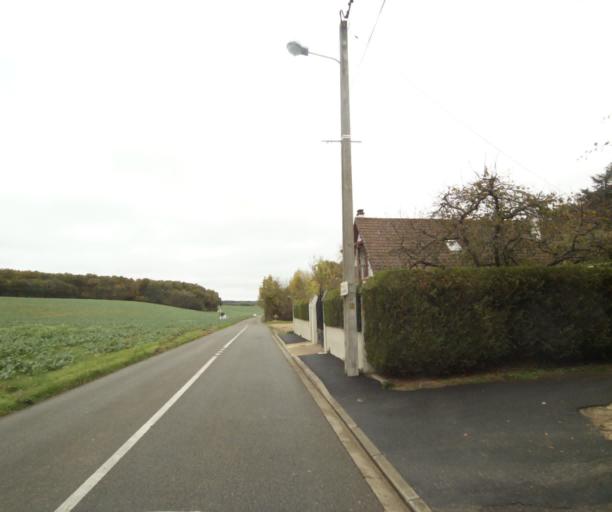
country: FR
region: Centre
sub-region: Departement d'Eure-et-Loir
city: Dreux
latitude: 48.7610
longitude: 1.3548
